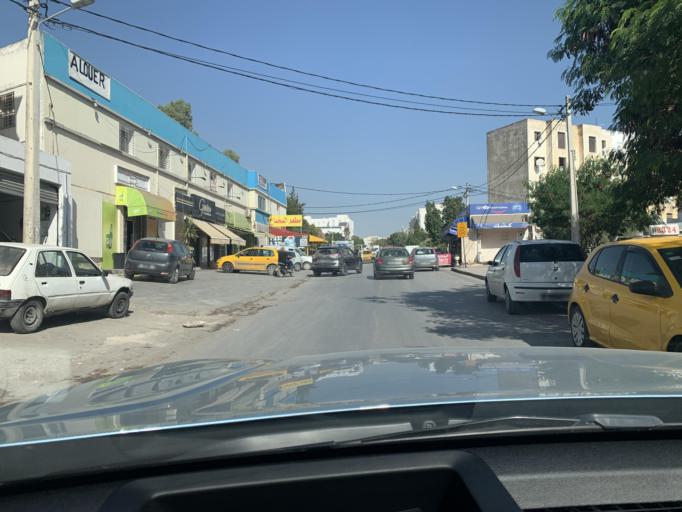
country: TN
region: Manouba
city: Manouba
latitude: 36.8275
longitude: 10.1214
